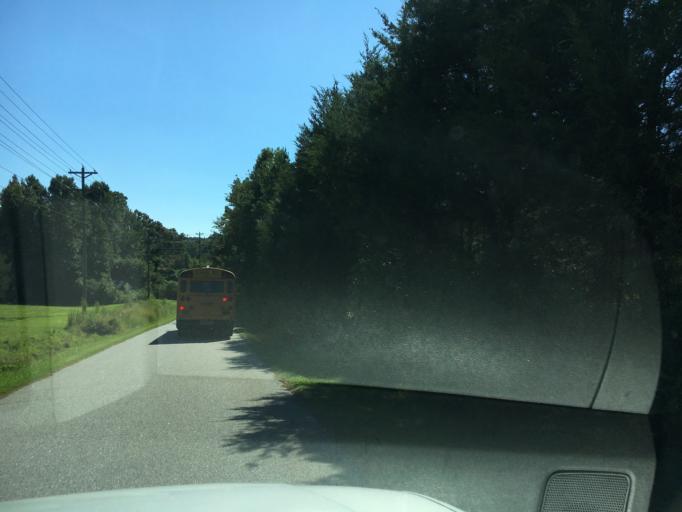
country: US
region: South Carolina
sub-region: Spartanburg County
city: Duncan
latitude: 34.8672
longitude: -82.1676
